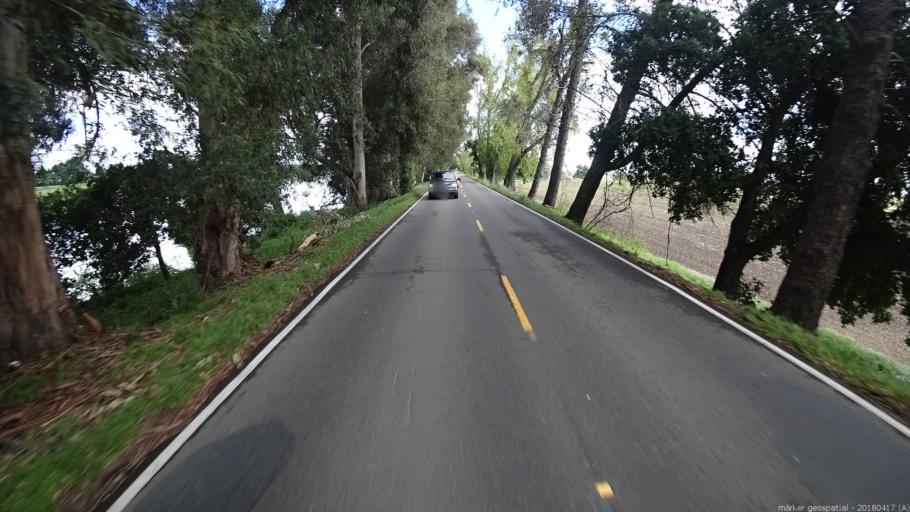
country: US
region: California
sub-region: Solano County
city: Rio Vista
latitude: 38.1747
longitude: -121.5906
